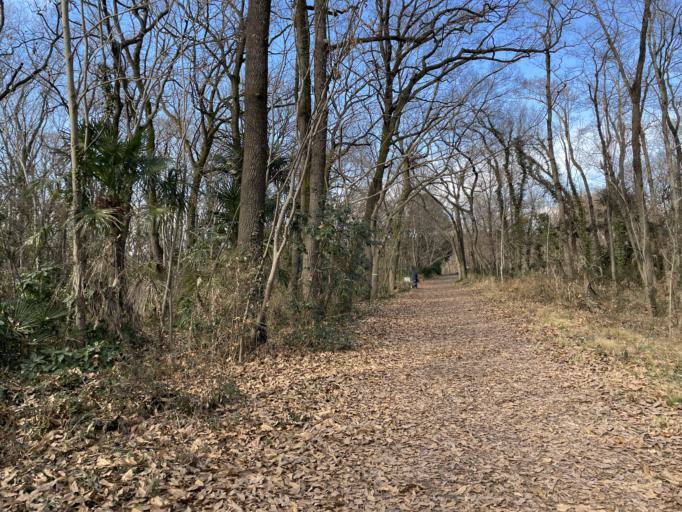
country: JP
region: Saitama
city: Shiki
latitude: 35.8574
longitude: 139.5962
